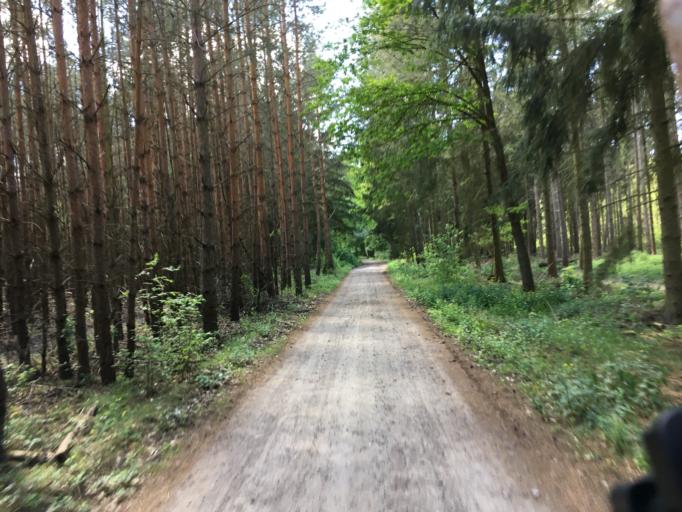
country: DE
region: Brandenburg
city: Trebbin
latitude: 52.1674
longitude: 13.2184
